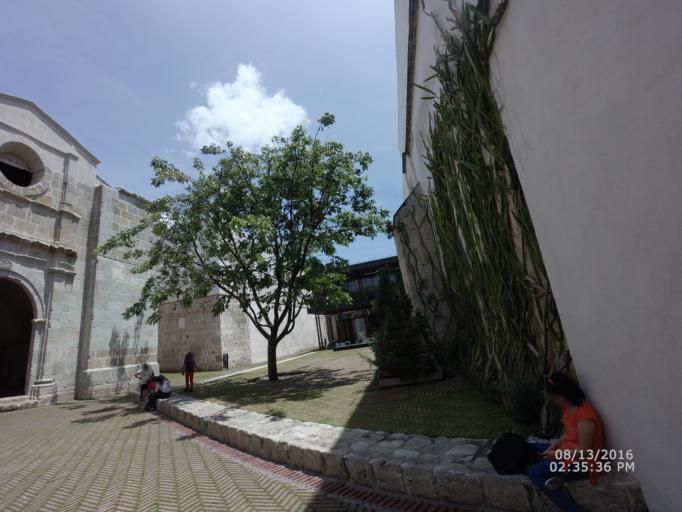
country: MX
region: Oaxaca
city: Oaxaca de Juarez
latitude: 17.0612
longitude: -96.7232
